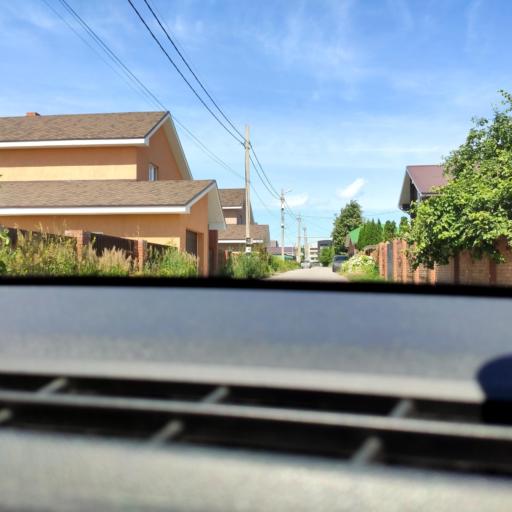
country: RU
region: Samara
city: Podstepki
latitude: 53.5077
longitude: 49.2389
